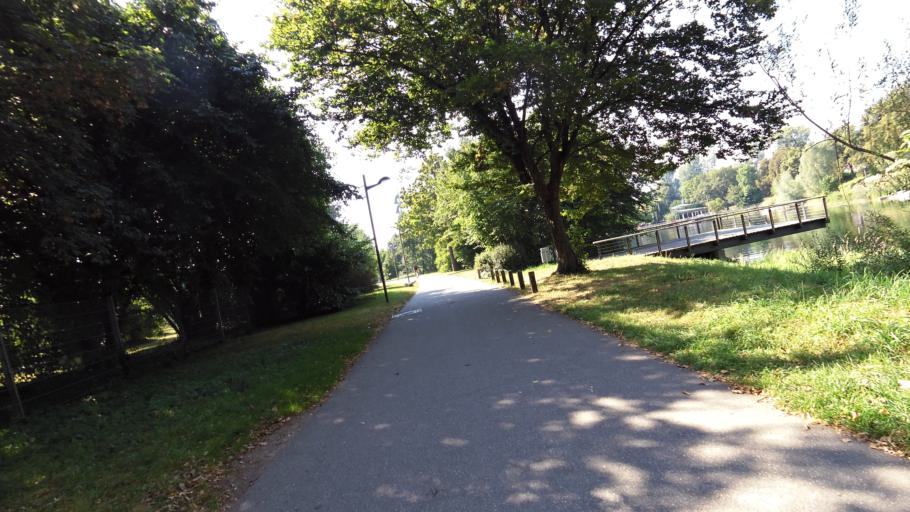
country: DE
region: Baden-Wuerttemberg
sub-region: Freiburg Region
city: Kehl
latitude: 48.5673
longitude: 7.8104
